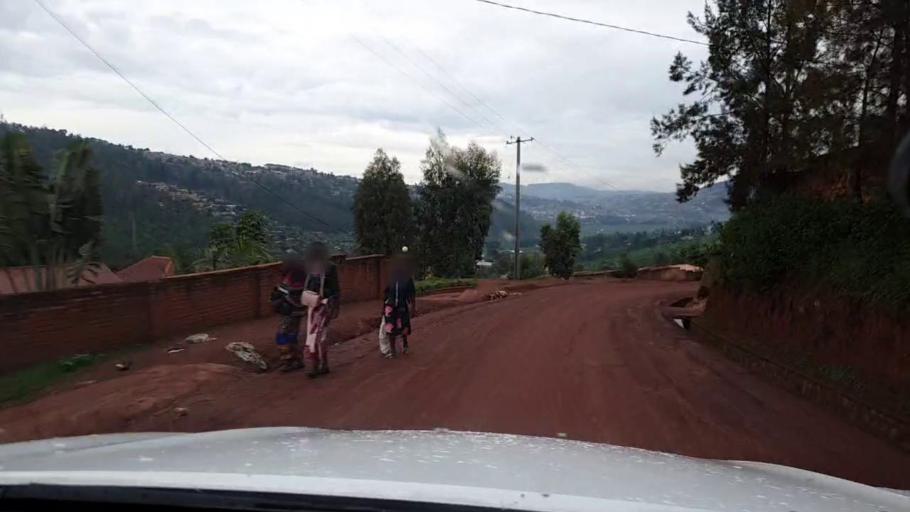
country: RW
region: Kigali
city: Kigali
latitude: -1.9064
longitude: 30.0463
